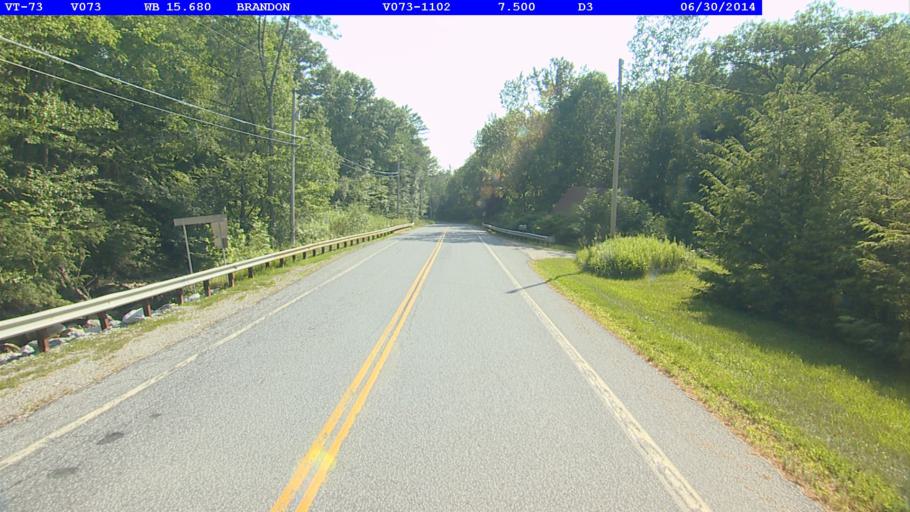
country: US
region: Vermont
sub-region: Rutland County
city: Brandon
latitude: 43.8416
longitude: -73.0299
